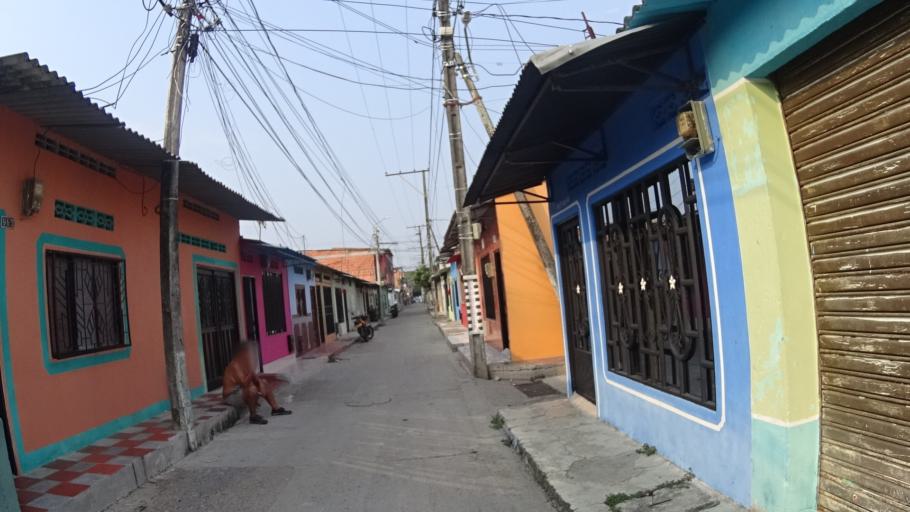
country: CO
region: Cundinamarca
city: Puerto Salgar
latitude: 5.4772
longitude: -74.6772
